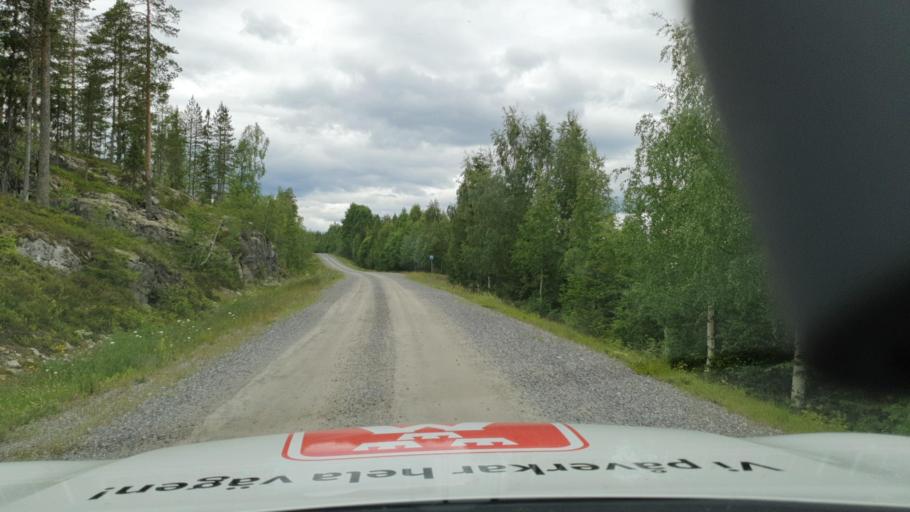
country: SE
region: Vaesterbotten
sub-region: Bjurholms Kommun
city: Bjurholm
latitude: 63.7592
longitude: 19.3656
